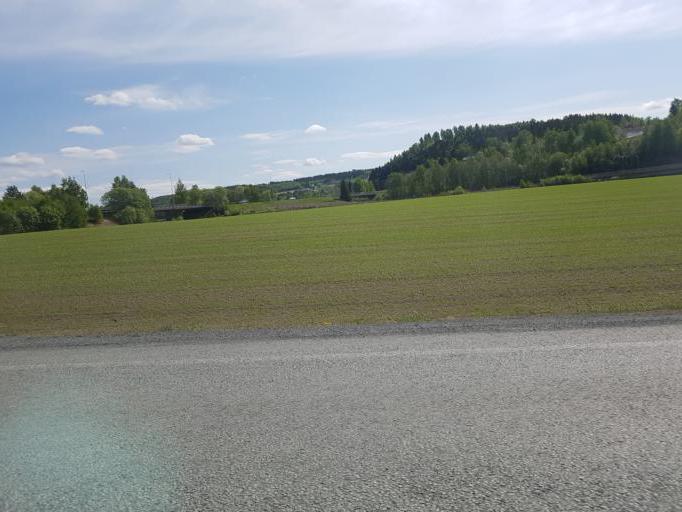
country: NO
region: Nord-Trondelag
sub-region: Levanger
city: Levanger
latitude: 63.7335
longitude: 11.2857
